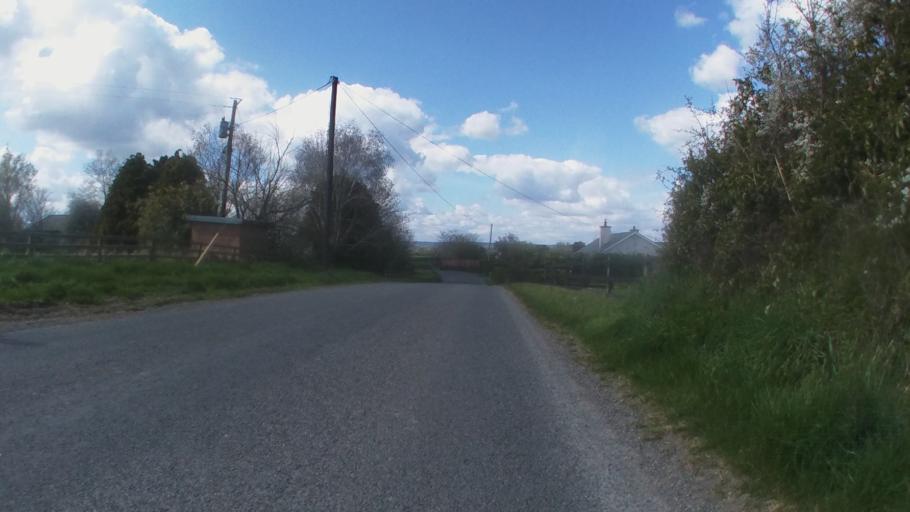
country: IE
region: Leinster
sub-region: Kilkenny
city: Kilkenny
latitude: 52.6605
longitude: -7.2114
